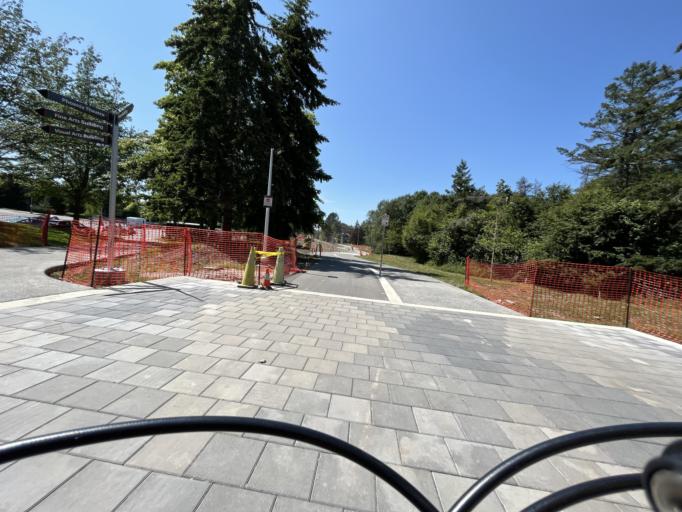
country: CA
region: British Columbia
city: Oak Bay
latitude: 48.4632
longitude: -123.3184
